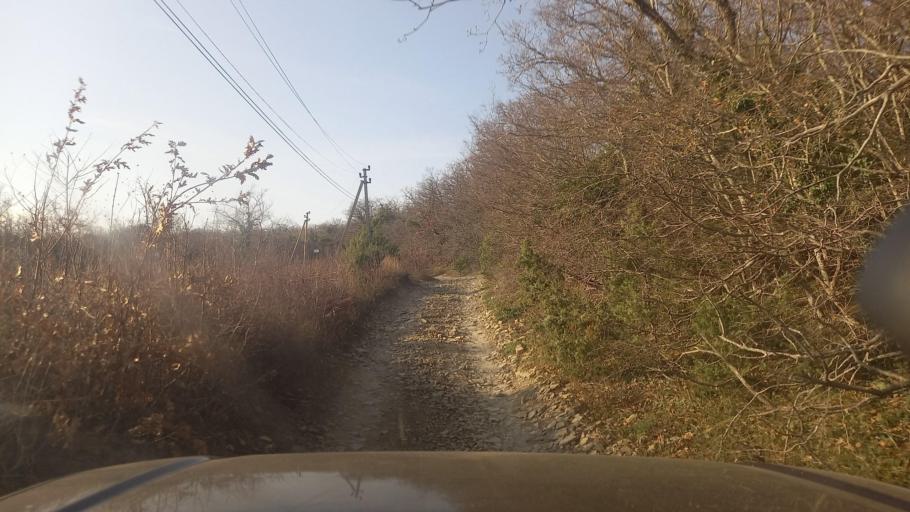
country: RU
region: Krasnodarskiy
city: Myskhako
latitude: 44.6667
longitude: 37.6760
